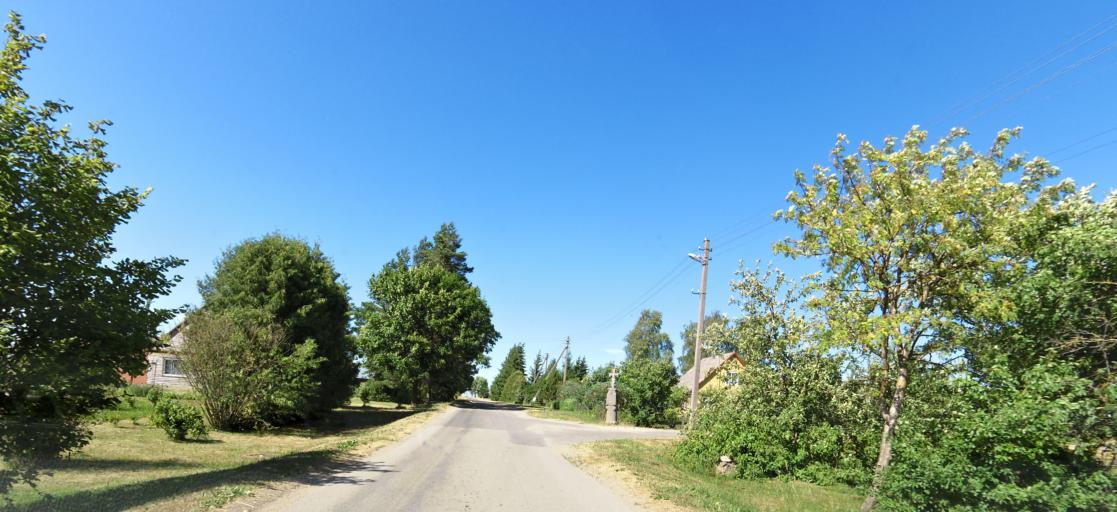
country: LT
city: Vabalninkas
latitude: 55.9750
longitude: 24.6623
